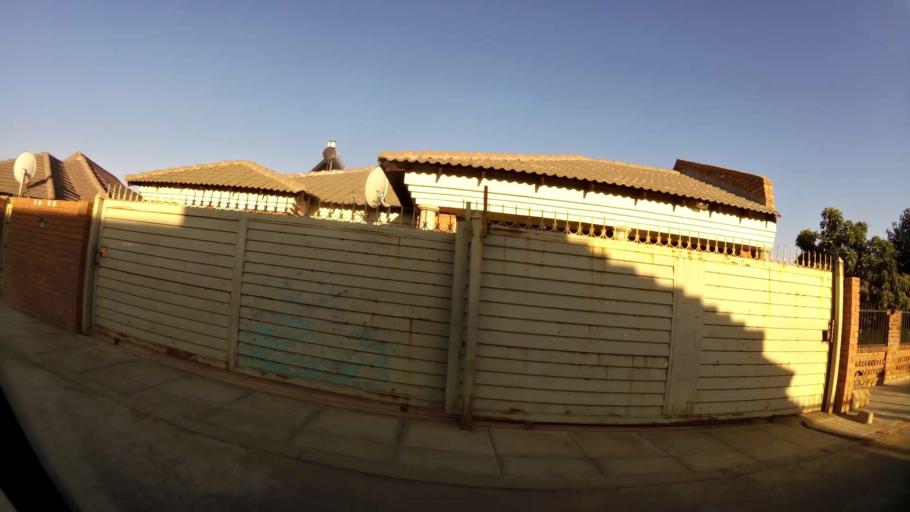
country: ZA
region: Gauteng
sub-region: City of Tshwane Metropolitan Municipality
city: Cullinan
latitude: -25.7247
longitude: 28.3952
